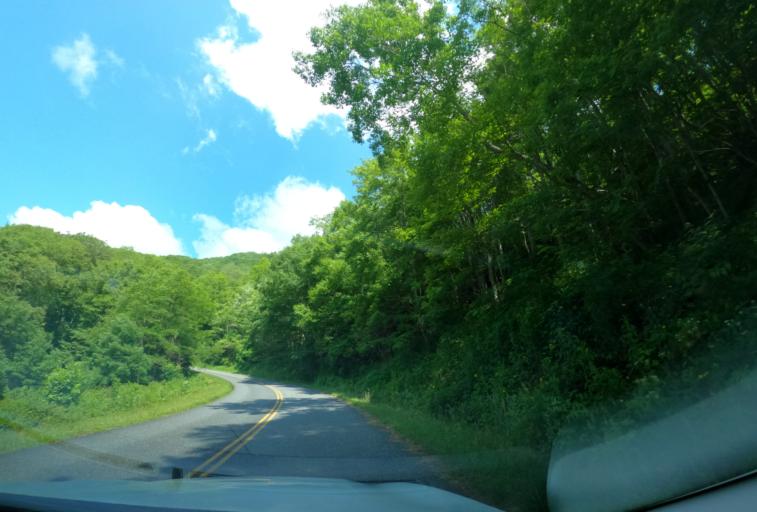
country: US
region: North Carolina
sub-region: Haywood County
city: Maggie Valley
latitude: 35.4539
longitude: -83.0940
